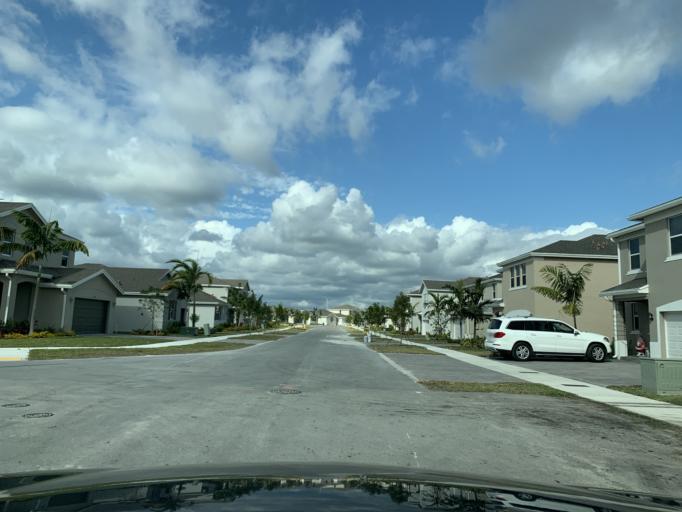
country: US
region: Florida
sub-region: Miami-Dade County
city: Naranja
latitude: 25.5106
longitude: -80.4090
